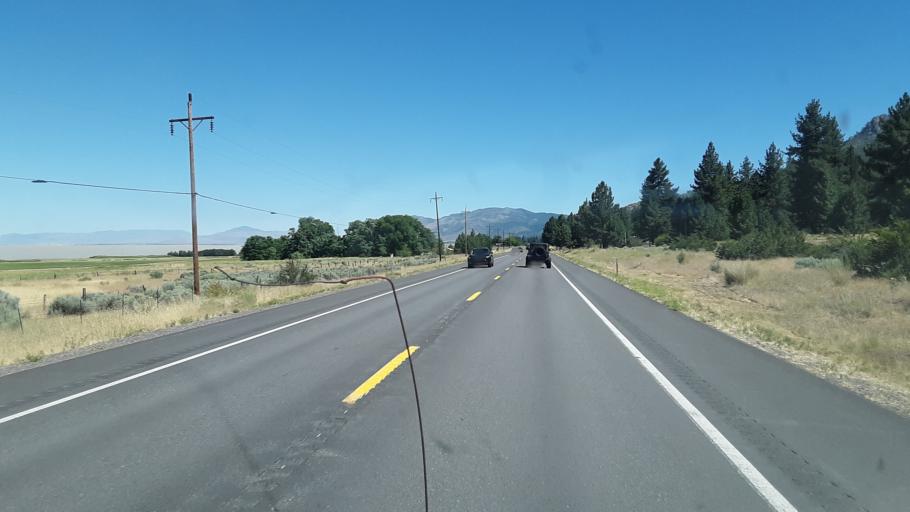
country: US
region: California
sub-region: Lassen County
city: Janesville
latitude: 40.2431
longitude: -120.4563
